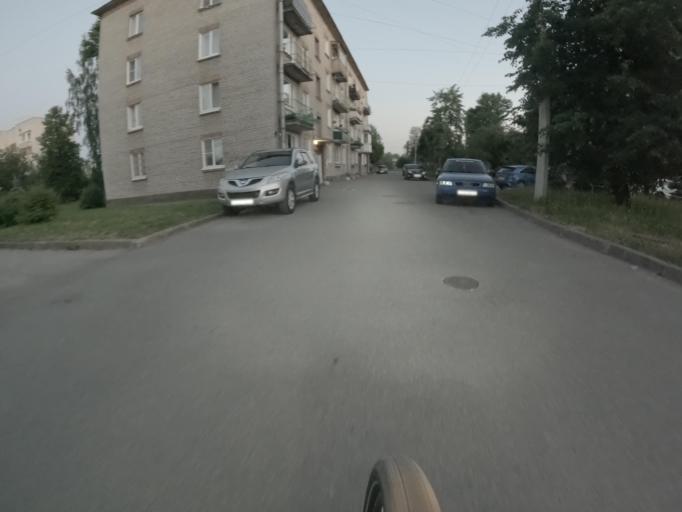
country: RU
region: St.-Petersburg
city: Sapernyy
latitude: 59.7782
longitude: 30.6939
